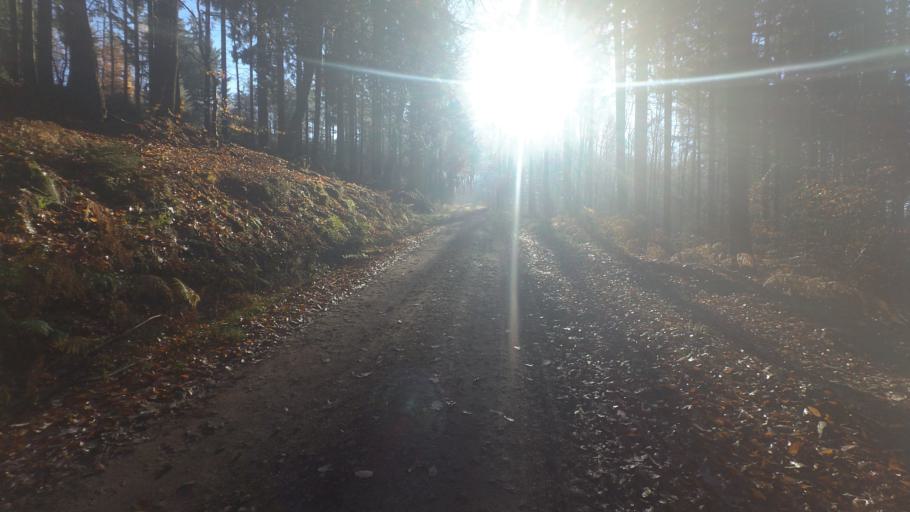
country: DE
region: Baden-Wuerttemberg
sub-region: Karlsruhe Region
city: Heddesbach
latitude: 49.4920
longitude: 8.8135
